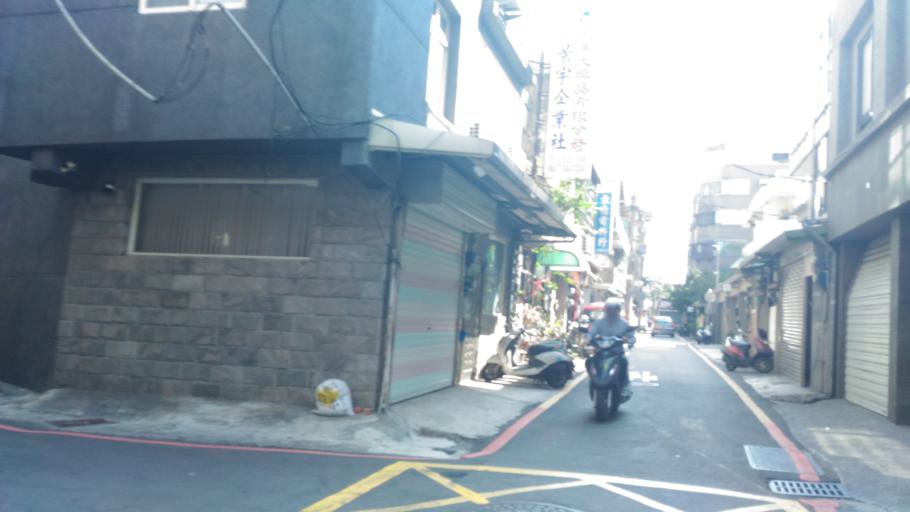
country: TW
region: Taiwan
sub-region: Hsinchu
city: Hsinchu
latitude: 24.8165
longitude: 120.9671
